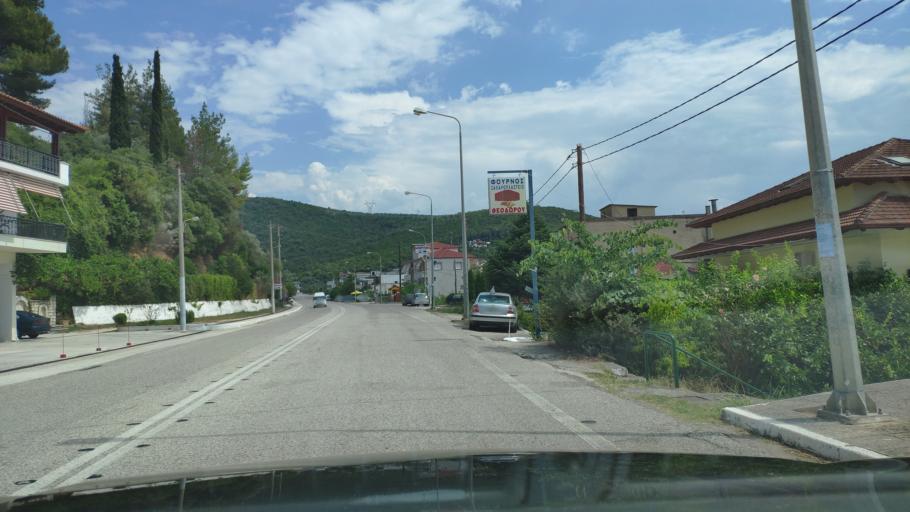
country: GR
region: West Greece
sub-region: Nomos Aitolias kai Akarnanias
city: Menidi
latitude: 39.0431
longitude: 21.1174
